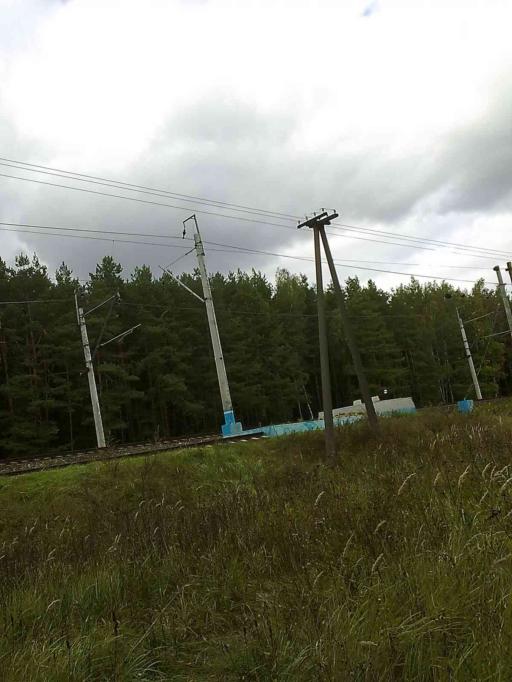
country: RU
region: Moscow
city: Tolstopal'tsevo
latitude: 55.6119
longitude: 37.1967
